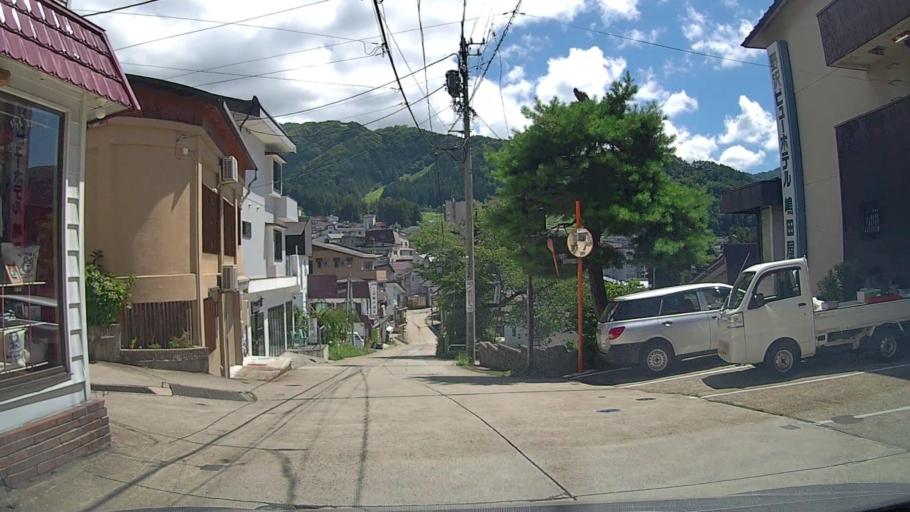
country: JP
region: Nagano
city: Iiyama
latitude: 36.9248
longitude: 138.4457
